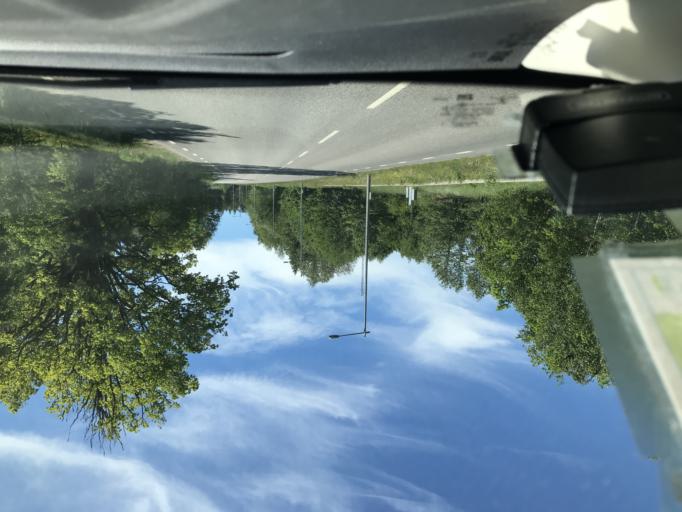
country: SE
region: Stockholm
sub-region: Botkyrka Kommun
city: Tumba
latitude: 59.2129
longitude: 17.8376
